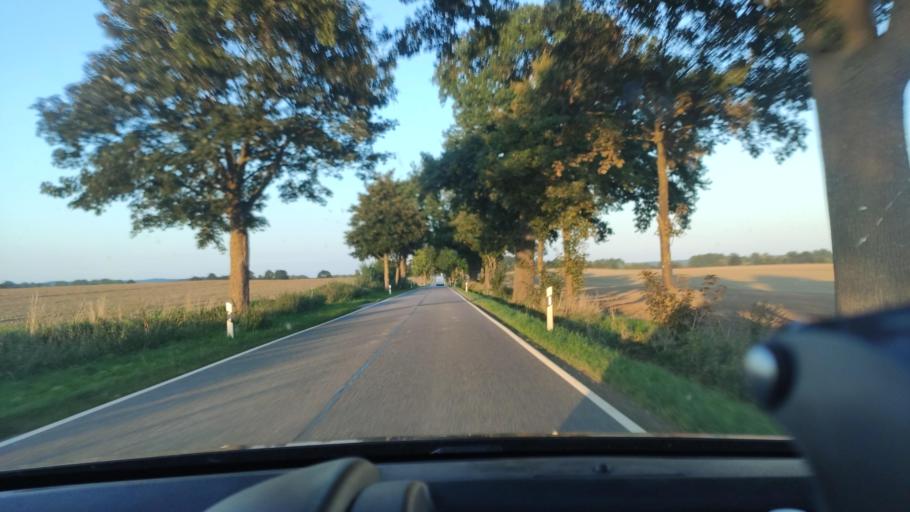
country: DE
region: Mecklenburg-Vorpommern
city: Gross Wokern
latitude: 53.6643
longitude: 12.5265
